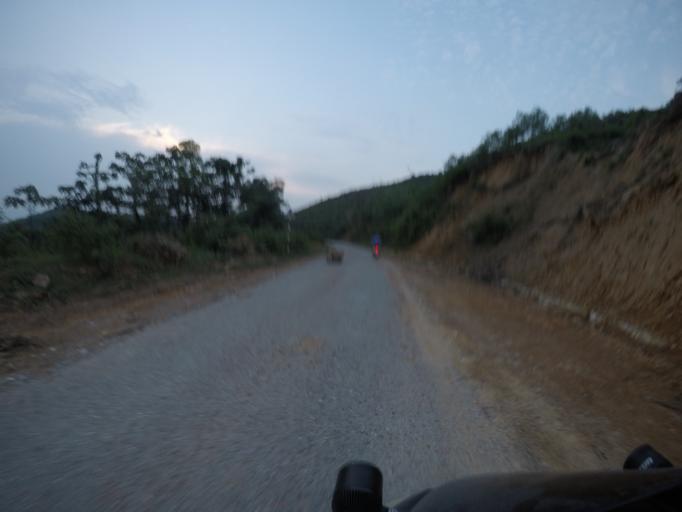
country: VN
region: Thai Nguyen
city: Chua Hang
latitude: 21.5837
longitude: 105.7122
